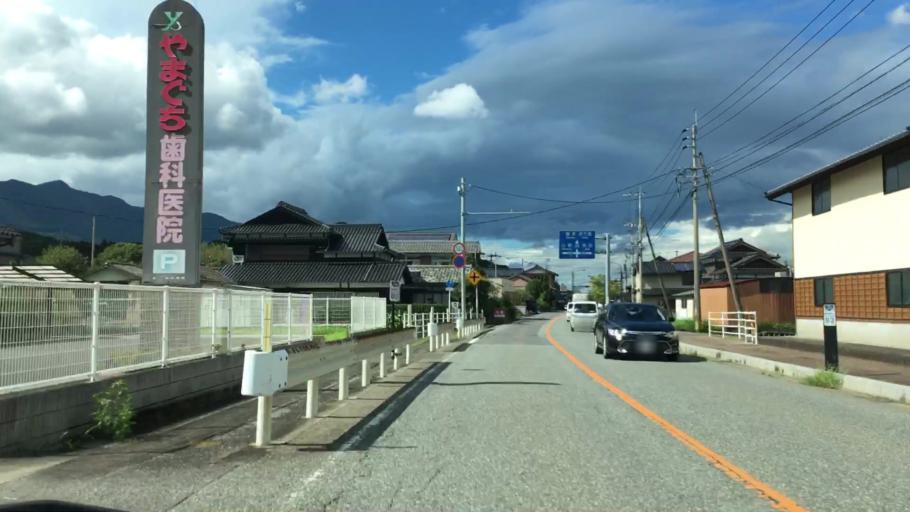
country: JP
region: Saga Prefecture
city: Imaricho-ko
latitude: 33.1939
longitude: 129.8508
